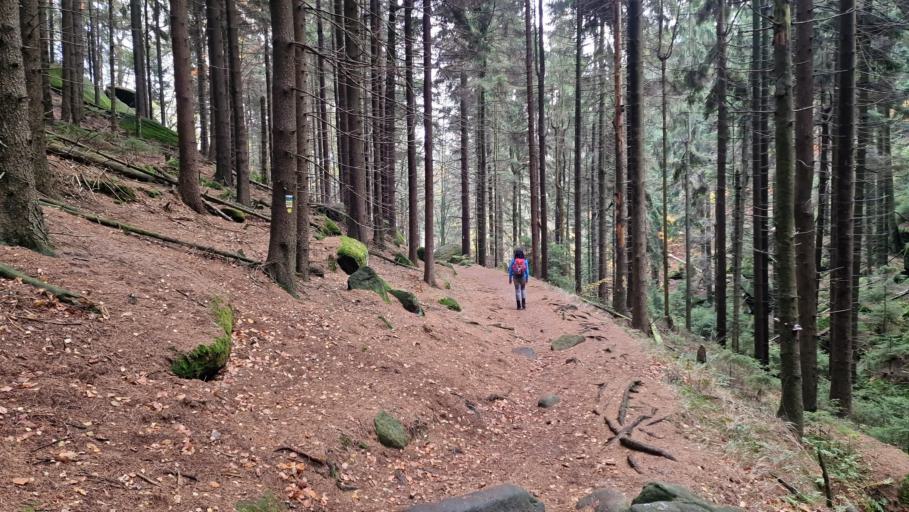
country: CZ
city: Machov
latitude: 50.5397
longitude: 16.2988
